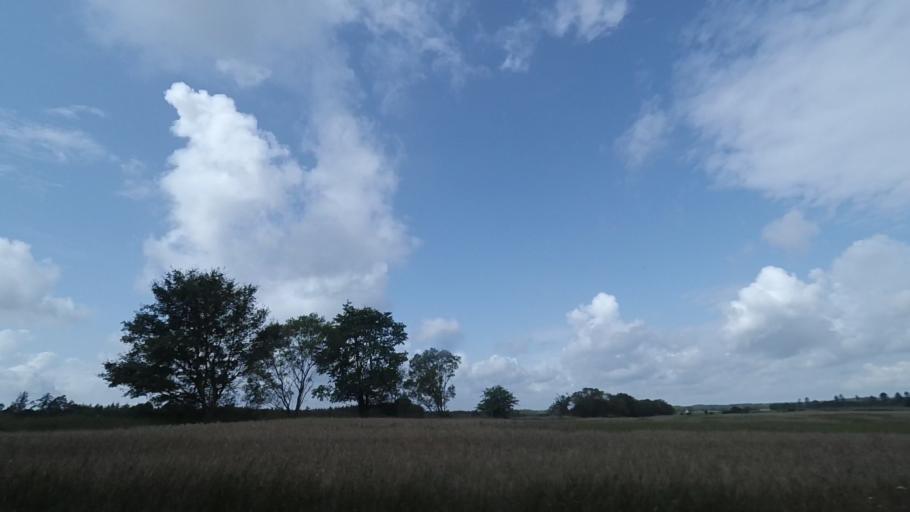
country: DK
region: Central Jutland
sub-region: Syddjurs Kommune
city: Ryomgard
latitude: 56.4382
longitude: 10.5605
